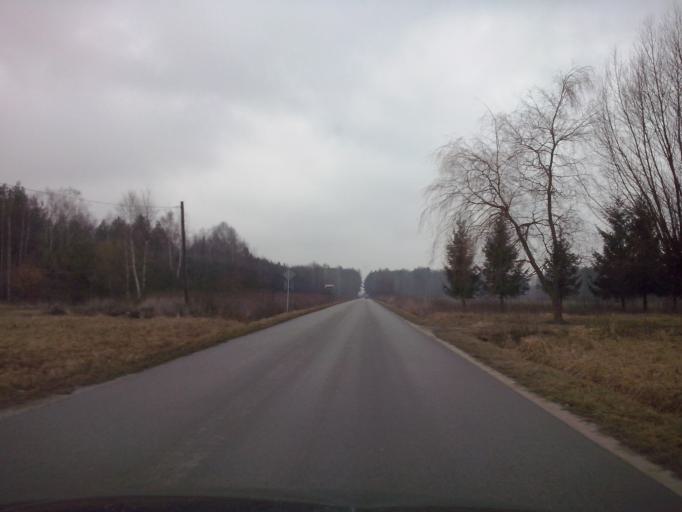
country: PL
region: Subcarpathian Voivodeship
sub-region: Powiat nizanski
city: Bieliny
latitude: 50.4513
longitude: 22.2860
